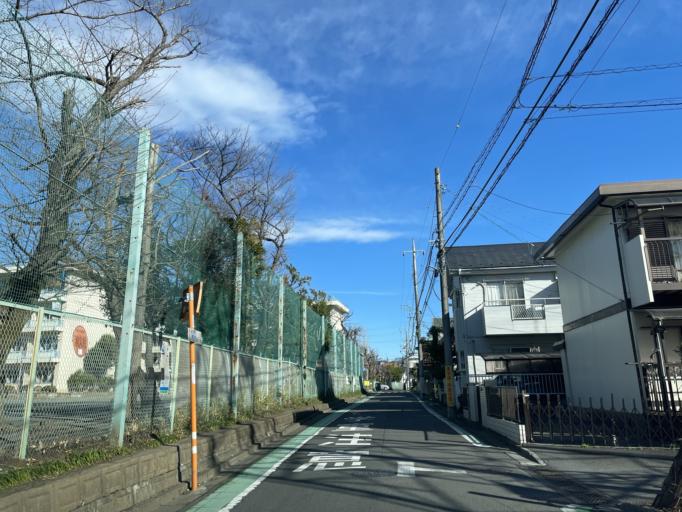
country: JP
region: Saitama
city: Tokorozawa
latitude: 35.7828
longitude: 139.4490
